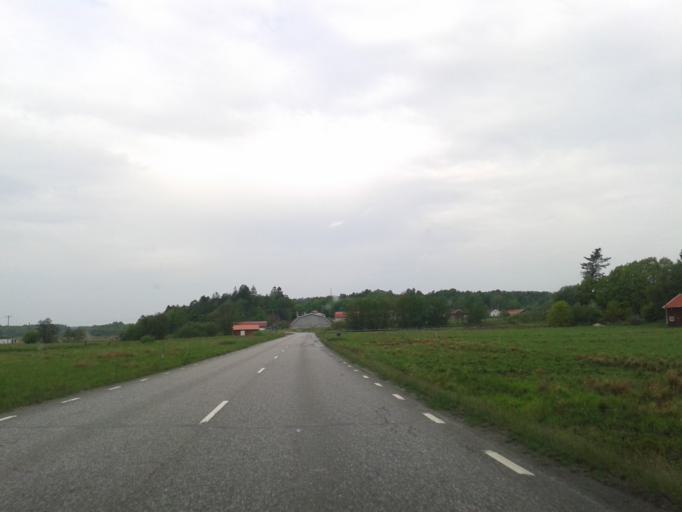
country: SE
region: Vaestra Goetaland
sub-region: Kungalvs Kommun
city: Kode
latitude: 57.8552
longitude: 11.8822
